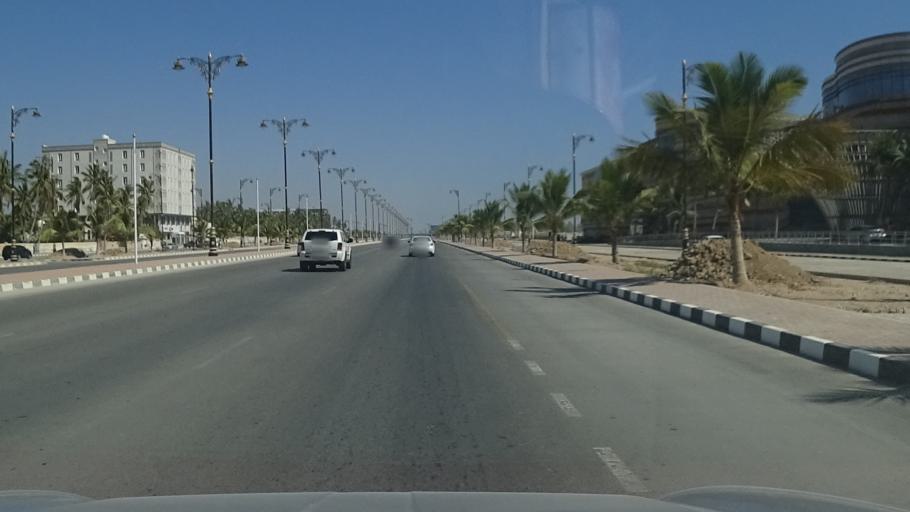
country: OM
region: Zufar
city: Salalah
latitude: 17.0361
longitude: 54.1634
